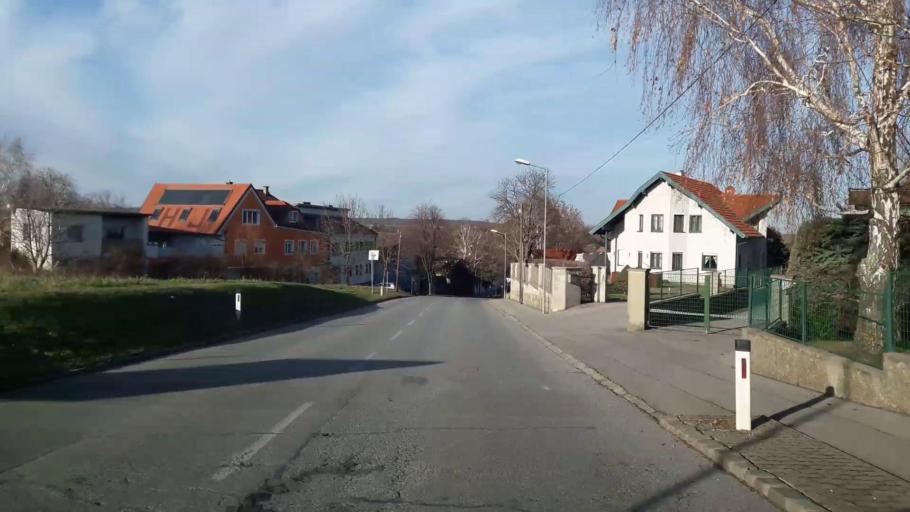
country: AT
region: Lower Austria
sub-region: Politischer Bezirk Ganserndorf
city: Auersthal
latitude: 48.3722
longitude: 16.6303
